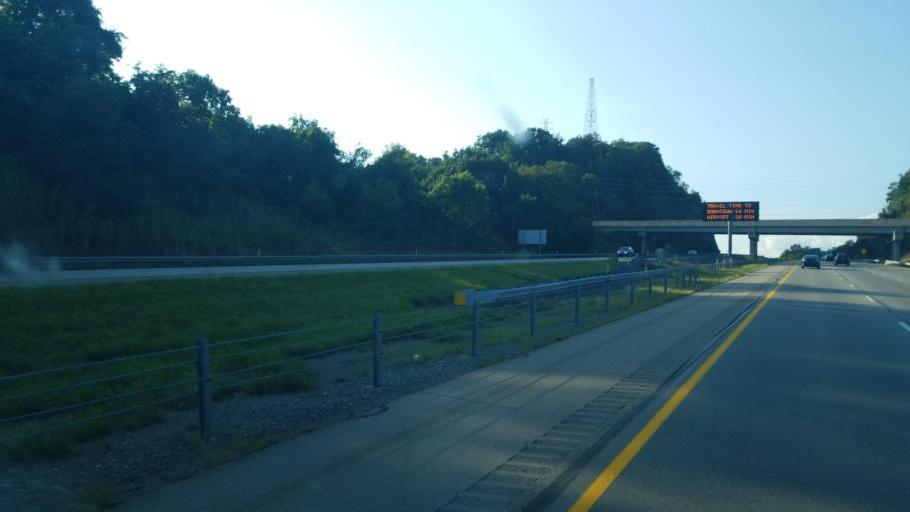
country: US
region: Pennsylvania
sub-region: Allegheny County
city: Heidelberg
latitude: 40.3883
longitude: -80.0984
